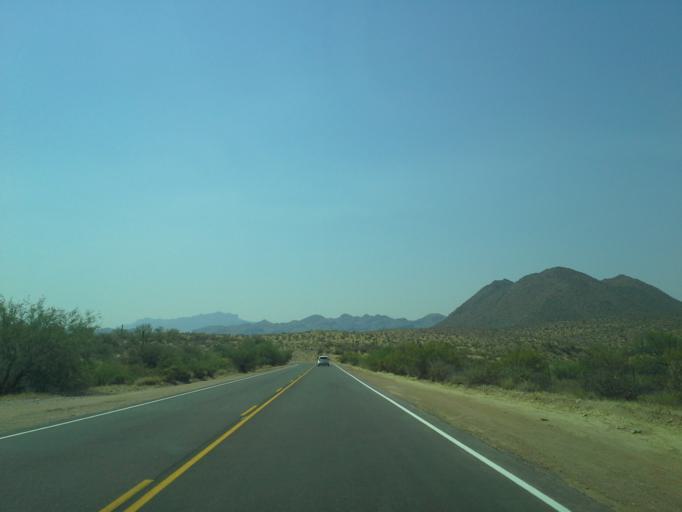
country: US
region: Arizona
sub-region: Maricopa County
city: Rio Verde
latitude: 33.6148
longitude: -111.5539
